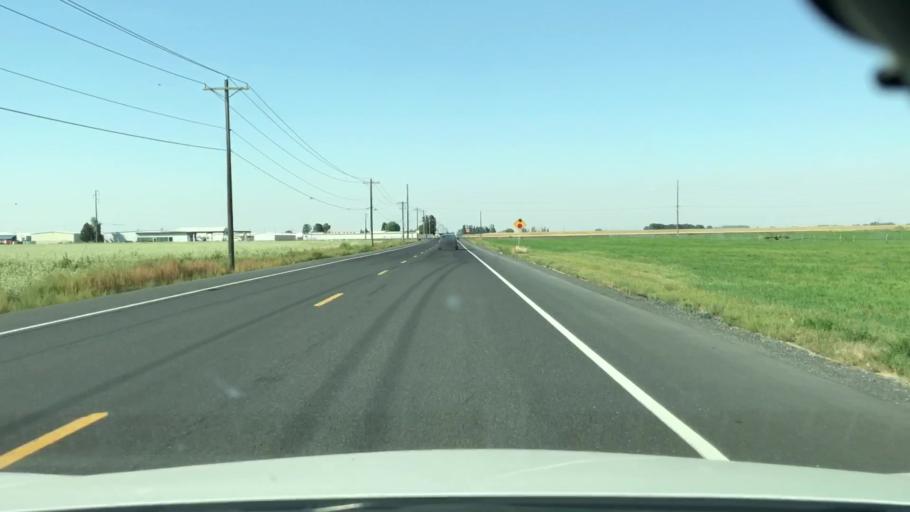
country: US
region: Washington
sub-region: Grant County
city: Moses Lake
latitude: 47.1282
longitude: -119.2358
